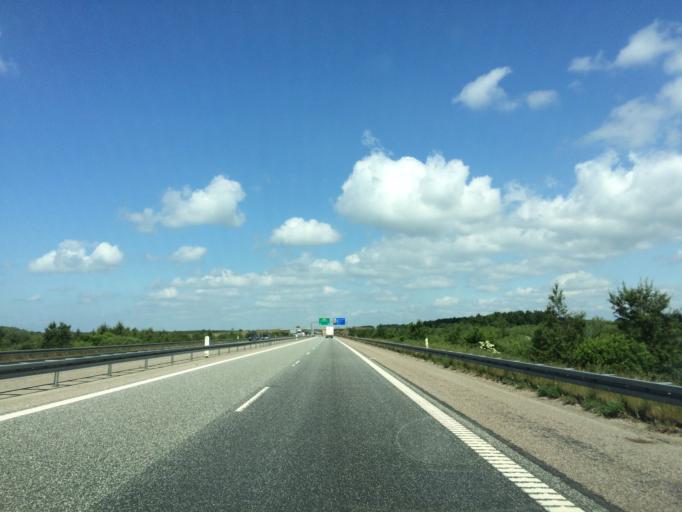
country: DK
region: Central Jutland
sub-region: Herning Kommune
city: Gjellerup Kirkeby
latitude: 56.1446
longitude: 9.0121
